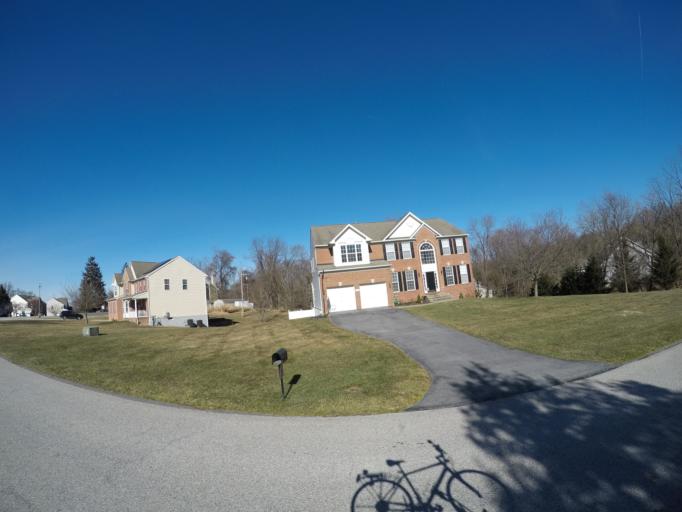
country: US
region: Maryland
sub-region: Howard County
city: Columbia
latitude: 39.2429
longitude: -76.8288
